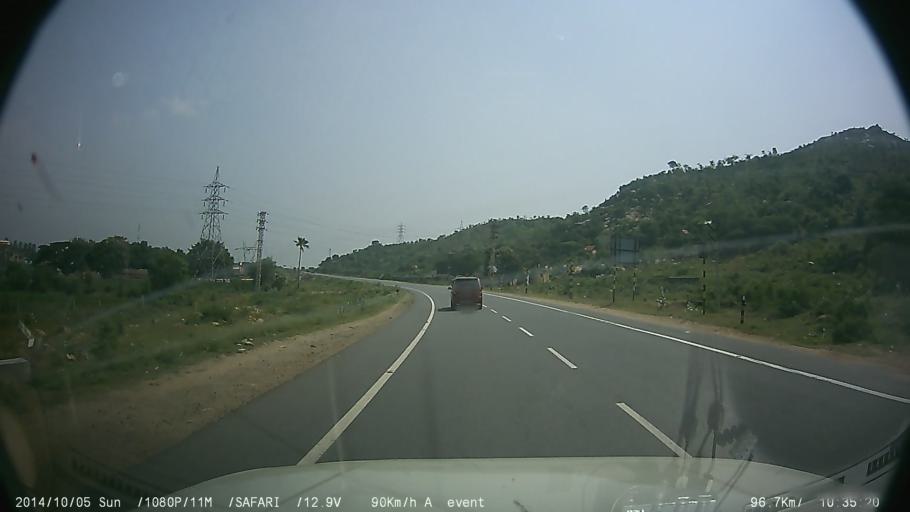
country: IN
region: Tamil Nadu
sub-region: Salem
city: Salem
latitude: 11.6567
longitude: 78.2040
